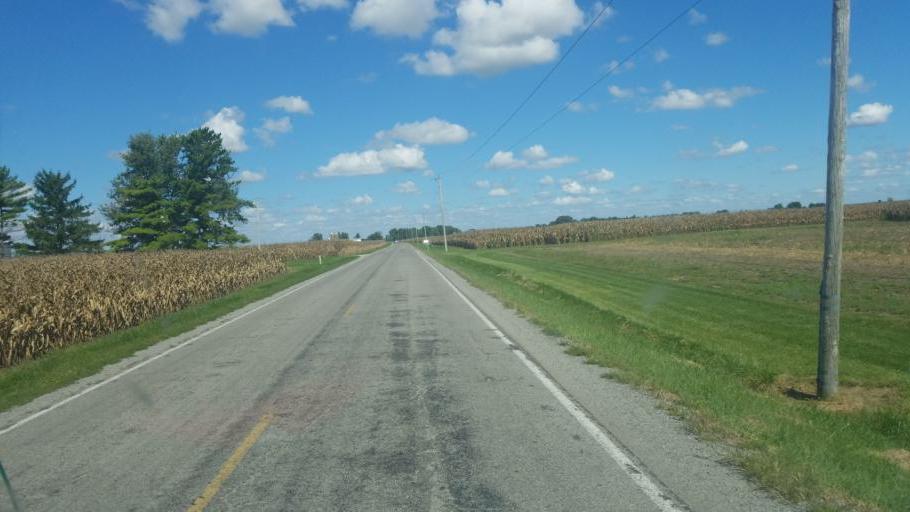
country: US
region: Ohio
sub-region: Madison County
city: Plain City
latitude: 40.0384
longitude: -83.3596
